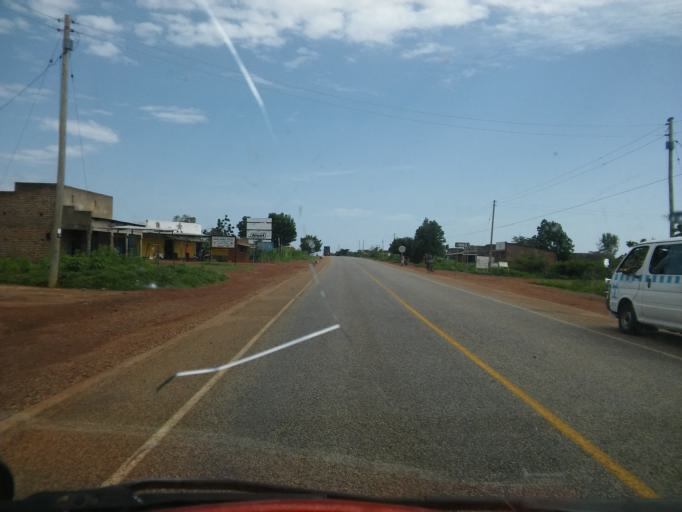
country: UG
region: Eastern Region
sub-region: Bukedea District
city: Bukedea
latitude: 1.2922
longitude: 34.0758
